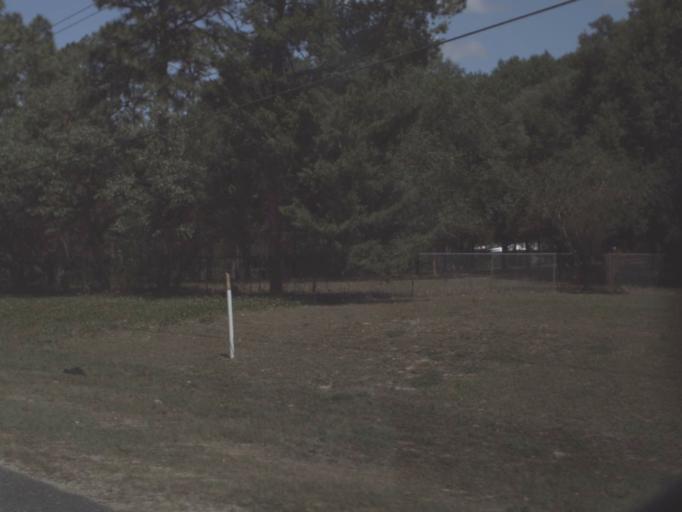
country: US
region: Florida
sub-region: Marion County
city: Silver Springs Shores
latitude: 29.1719
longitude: -81.8605
